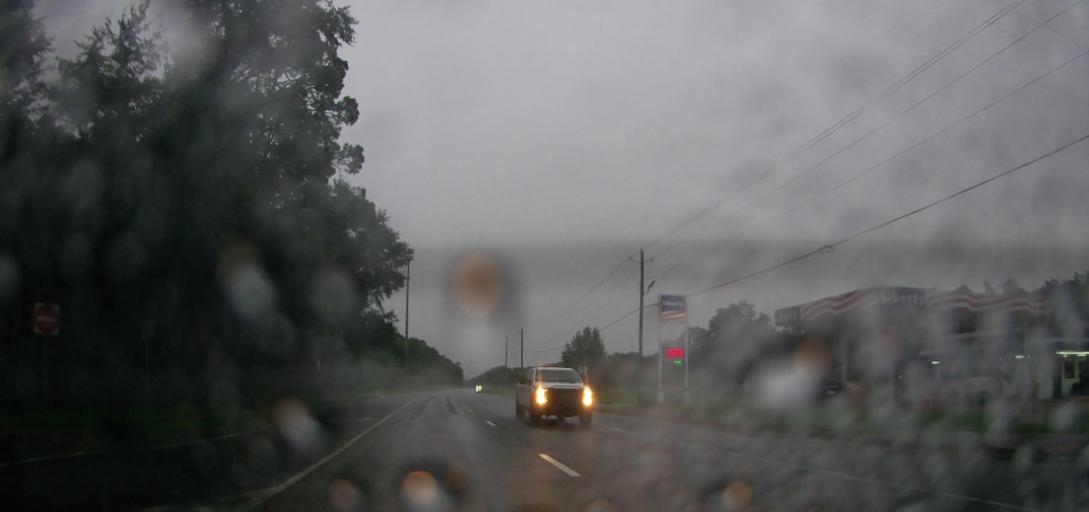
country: US
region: Georgia
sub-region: Clinch County
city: Homerville
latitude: 31.0391
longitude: -82.7409
